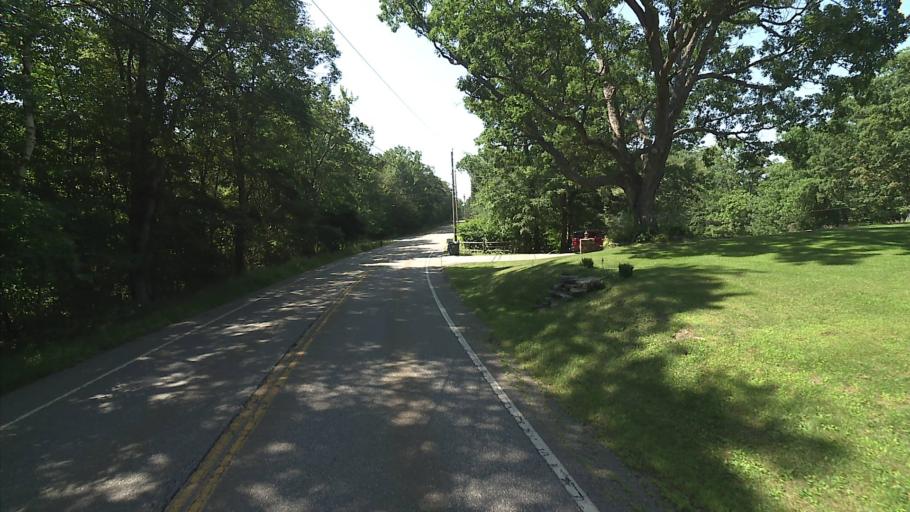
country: US
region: Connecticut
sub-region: Litchfield County
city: New Preston
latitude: 41.7727
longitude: -73.3529
